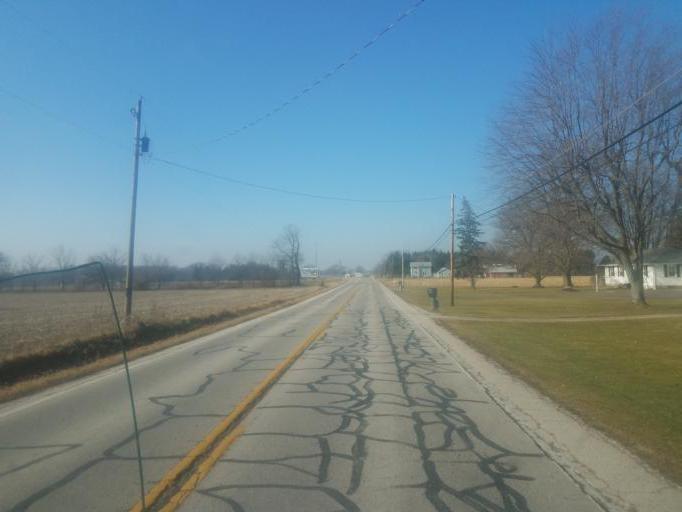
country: US
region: Ohio
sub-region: Seneca County
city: Tiffin
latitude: 41.1243
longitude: -83.1345
